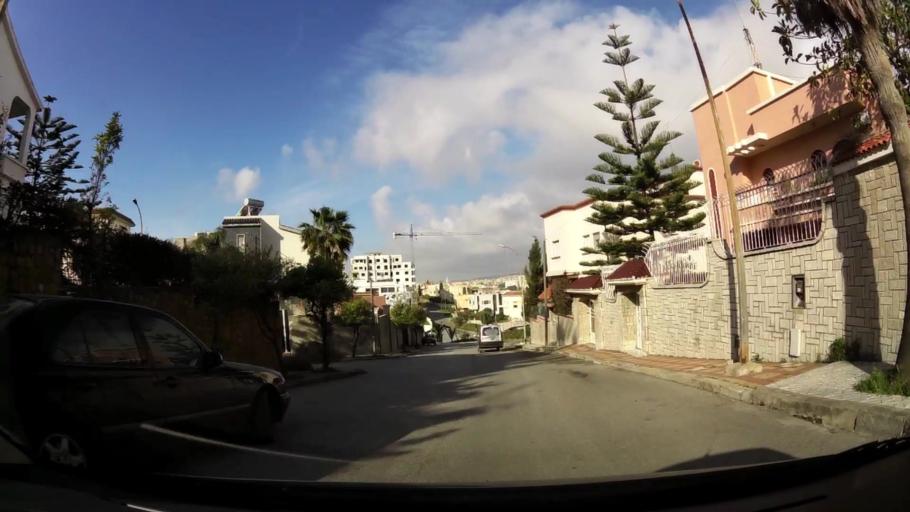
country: MA
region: Tanger-Tetouan
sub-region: Tanger-Assilah
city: Tangier
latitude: 35.7668
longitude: -5.7981
